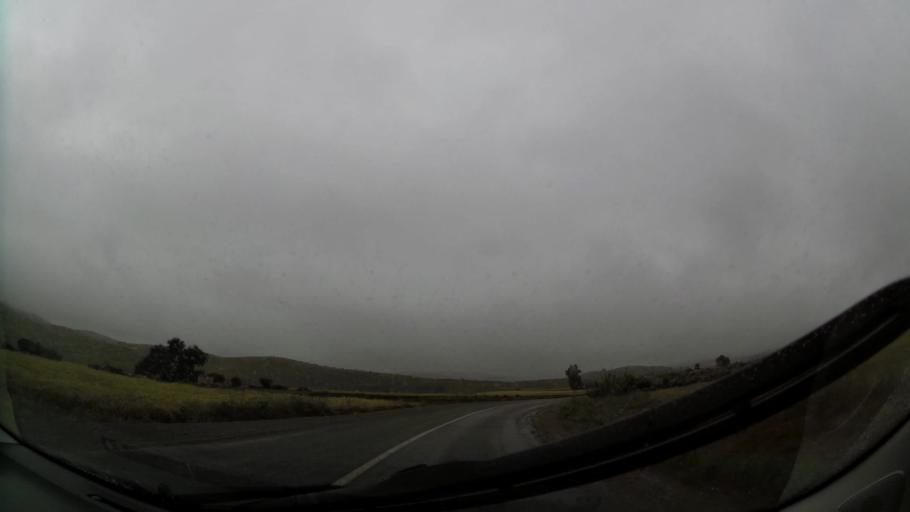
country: MA
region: Oriental
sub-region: Nador
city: Boudinar
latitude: 35.1107
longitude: -3.5732
